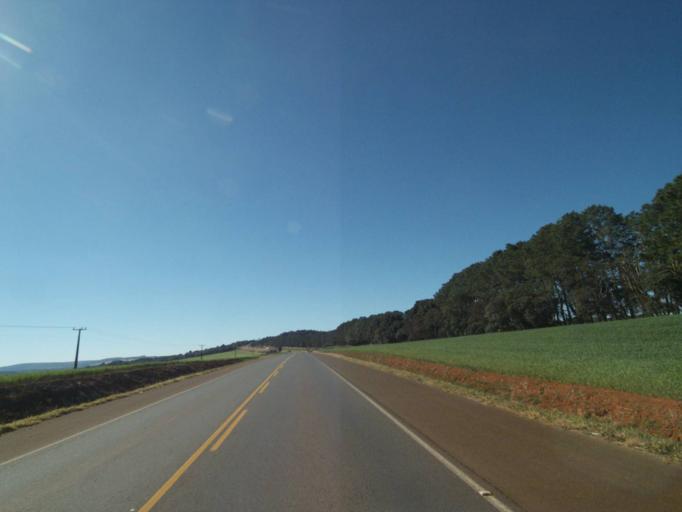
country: BR
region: Parana
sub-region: Tibagi
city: Tibagi
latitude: -24.4195
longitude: -50.3706
